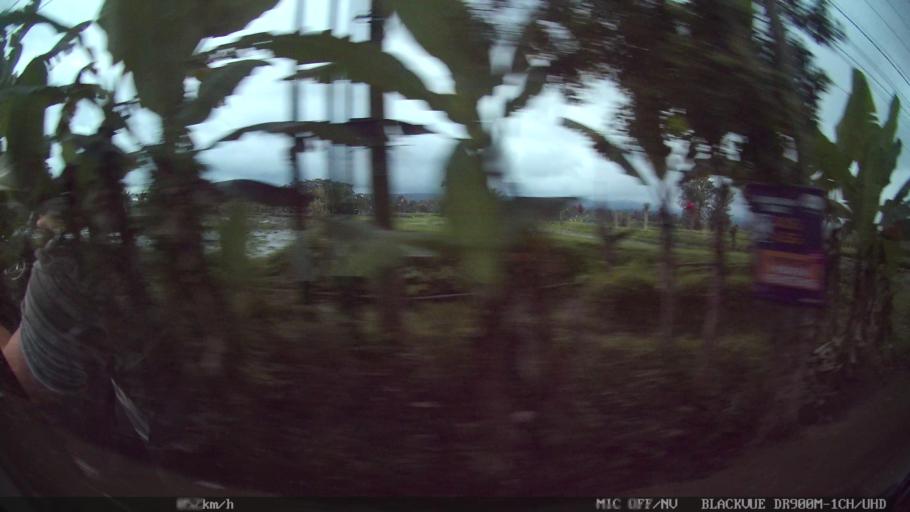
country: ID
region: Bali
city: Penebel
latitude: -8.4074
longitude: 115.1462
